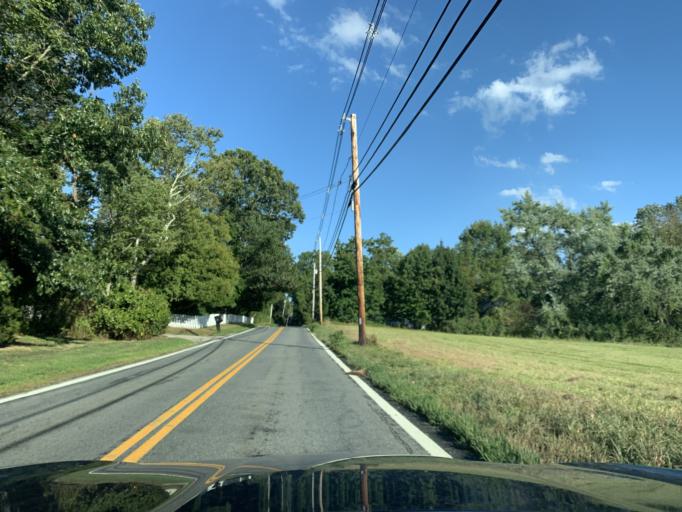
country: US
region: Rhode Island
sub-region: Washington County
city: Exeter
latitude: 41.5456
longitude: -71.5258
